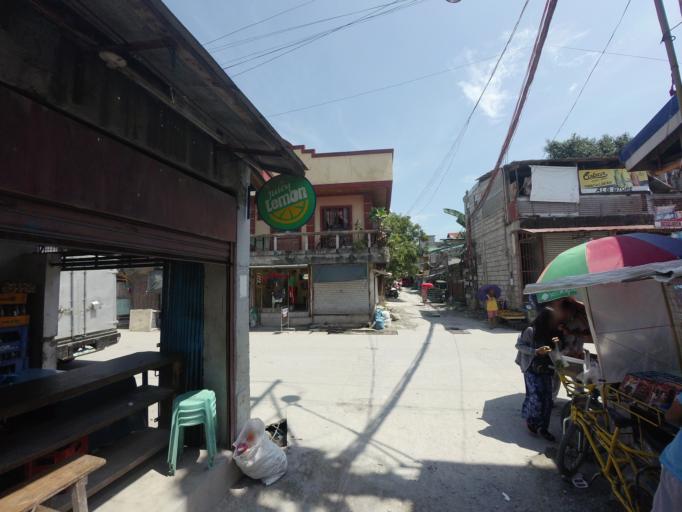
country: PH
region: Calabarzon
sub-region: Province of Rizal
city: Taytay
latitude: 14.5386
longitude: 121.1103
